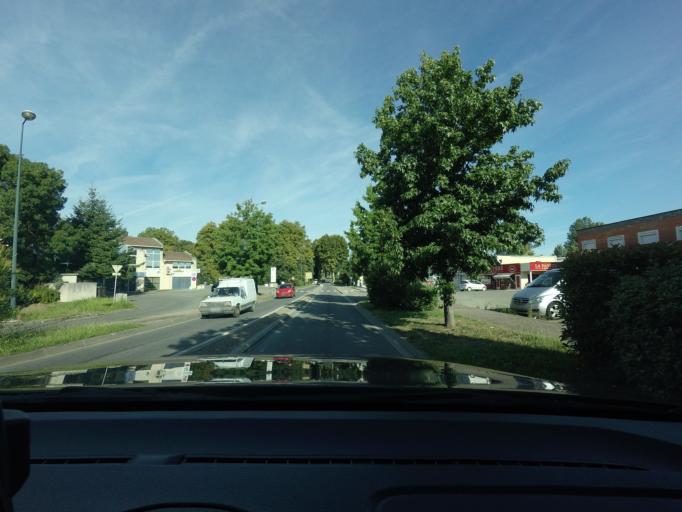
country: FR
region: Midi-Pyrenees
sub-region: Departement de la Haute-Garonne
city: Cornebarrieu
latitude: 43.6526
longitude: 1.3285
